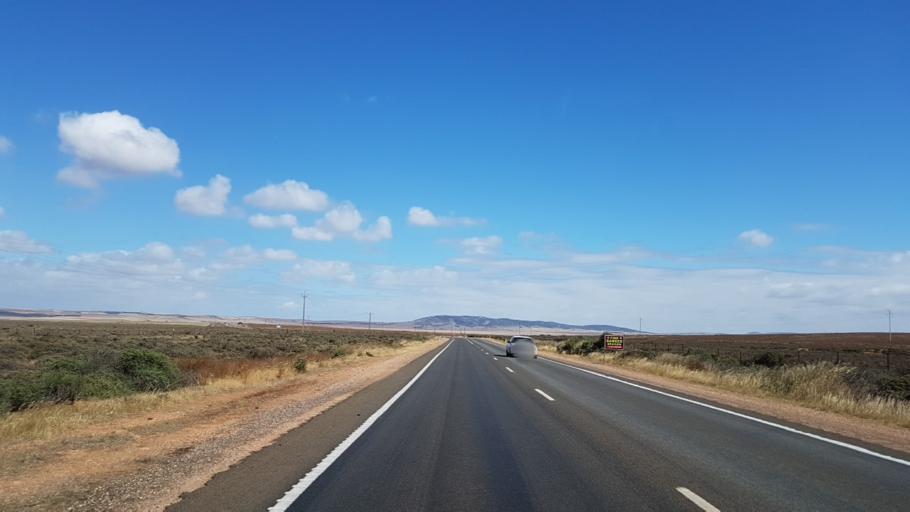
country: AU
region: South Australia
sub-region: Wakefield
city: Balaklava
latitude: -34.1270
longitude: 138.1394
